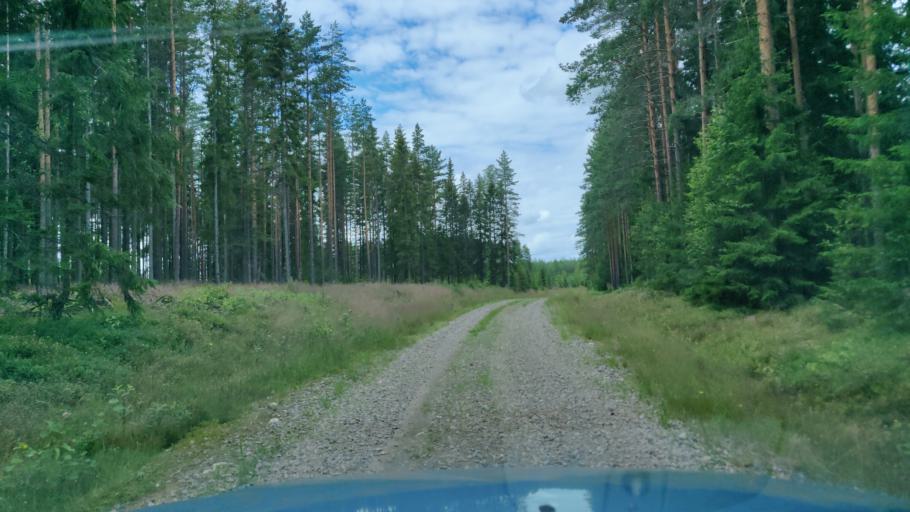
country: SE
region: Vaermland
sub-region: Hagfors Kommun
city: Hagfors
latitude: 59.9615
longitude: 13.5873
